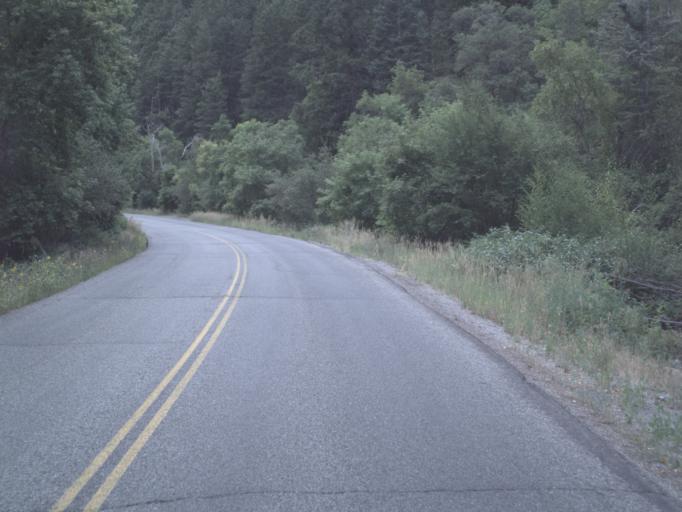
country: US
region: Utah
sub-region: Utah County
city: Orem
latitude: 40.3728
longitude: -111.5689
